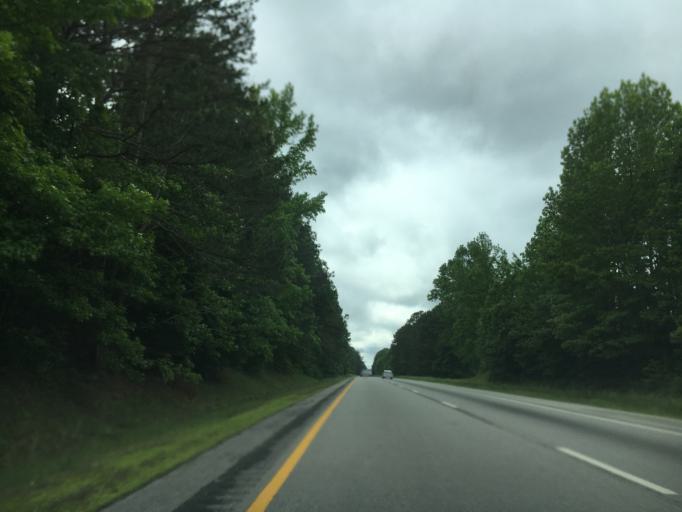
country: US
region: Virginia
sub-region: Mecklenburg County
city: South Hill
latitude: 36.7731
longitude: -78.0405
